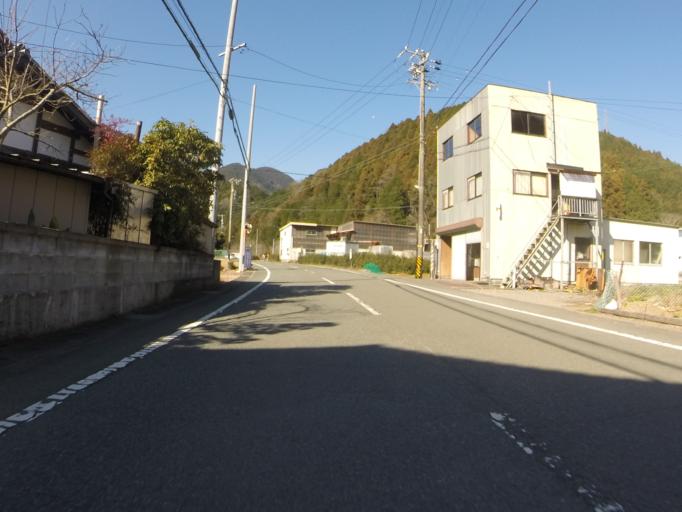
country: JP
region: Shizuoka
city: Fujinomiya
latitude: 35.1243
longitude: 138.4789
